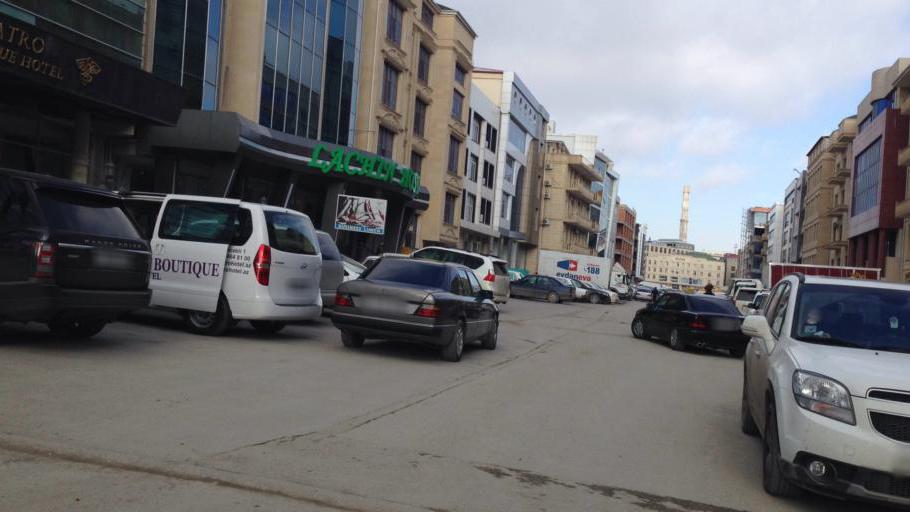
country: AZ
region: Baki
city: Baku
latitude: 40.4099
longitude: 49.8626
